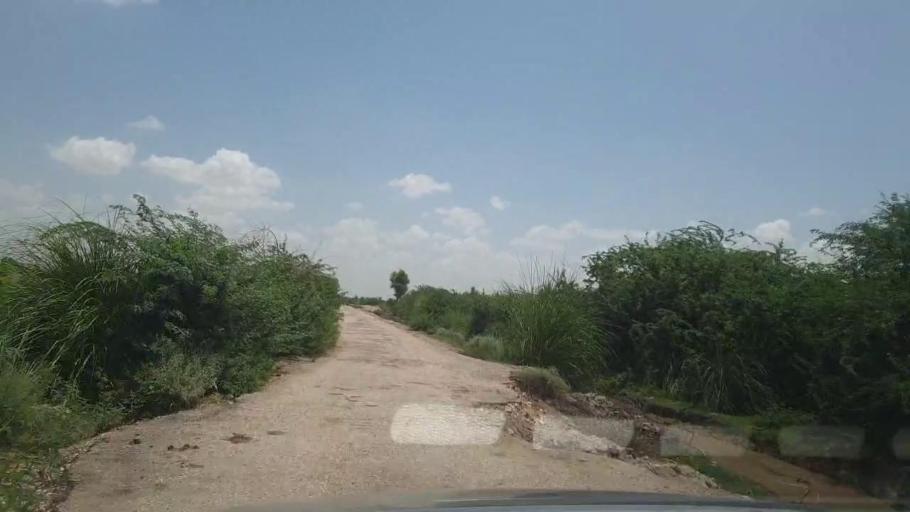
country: PK
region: Sindh
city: Kot Diji
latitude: 27.2914
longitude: 69.0864
